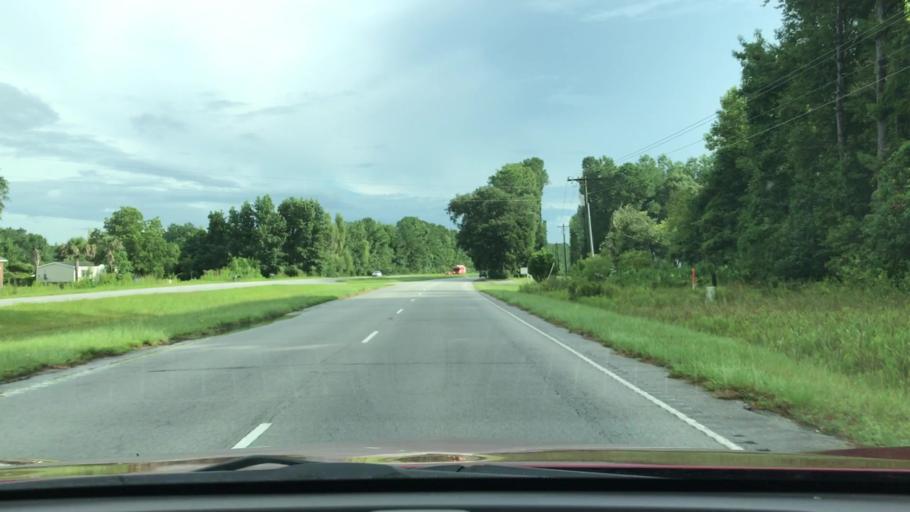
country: US
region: South Carolina
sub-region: Charleston County
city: Awendaw
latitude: 33.0004
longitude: -79.6438
